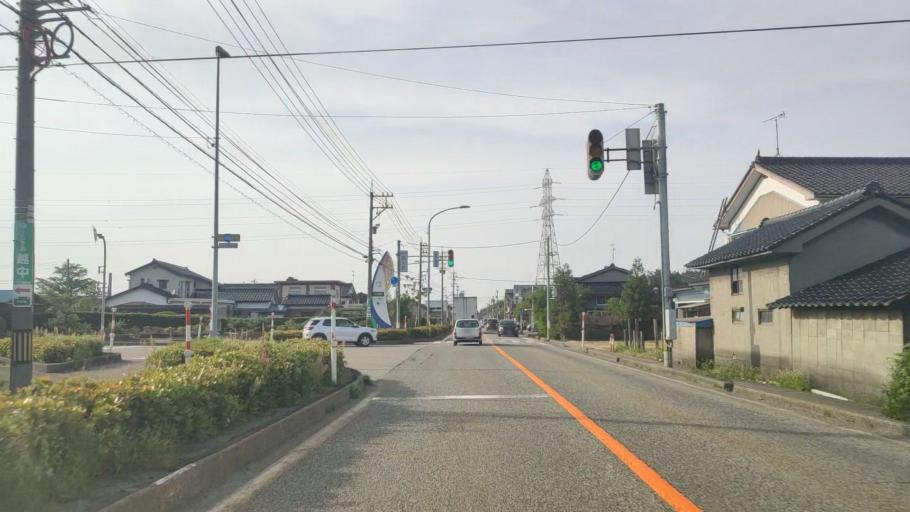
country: JP
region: Toyama
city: Yatsuomachi-higashikumisaka
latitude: 36.5676
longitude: 137.2106
